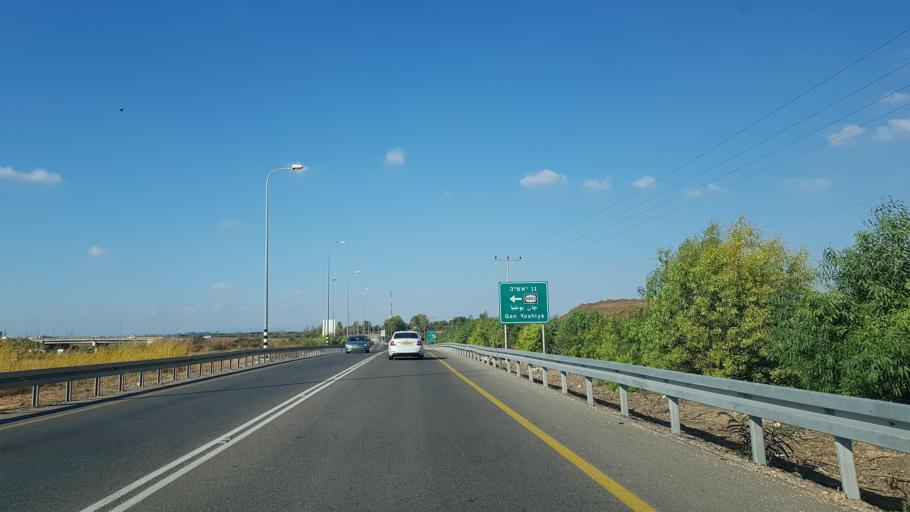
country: PS
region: West Bank
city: Tulkarm
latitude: 32.3427
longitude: 35.0109
